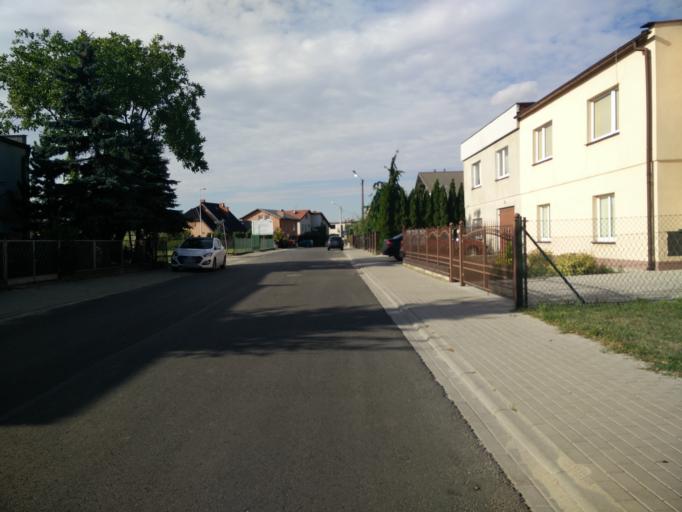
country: PL
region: Greater Poland Voivodeship
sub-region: Powiat sredzki
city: Sroda Wielkopolska
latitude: 52.2332
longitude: 17.2543
